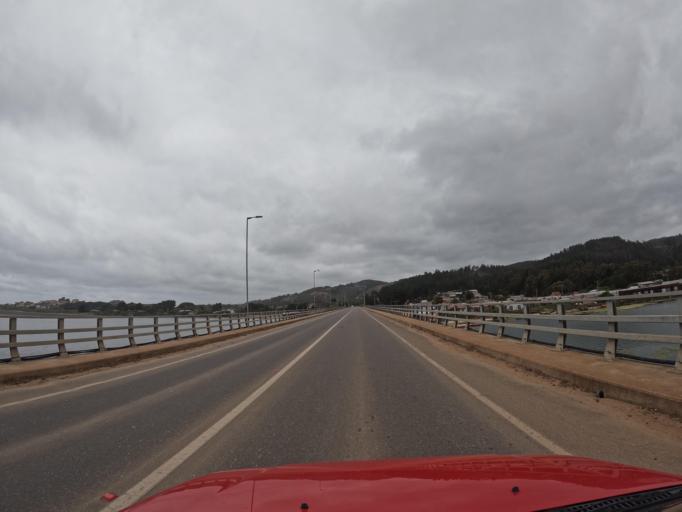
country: CL
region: O'Higgins
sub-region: Provincia de Colchagua
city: Santa Cruz
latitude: -34.4807
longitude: -72.0183
